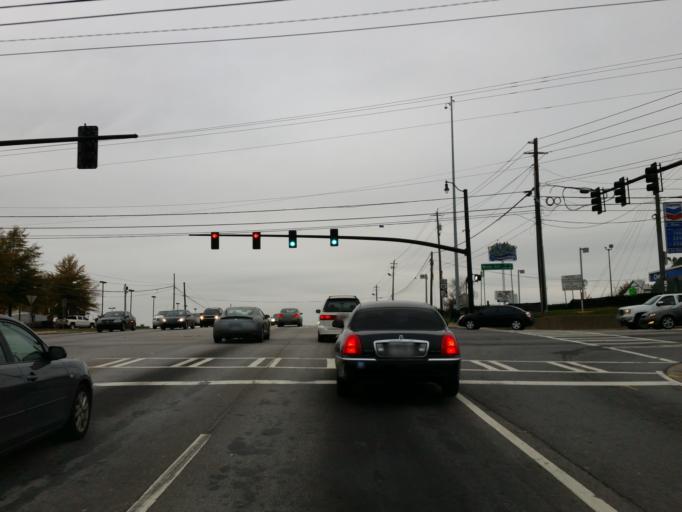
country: US
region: Georgia
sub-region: Cobb County
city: Smyrna
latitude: 33.9026
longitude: -84.4870
